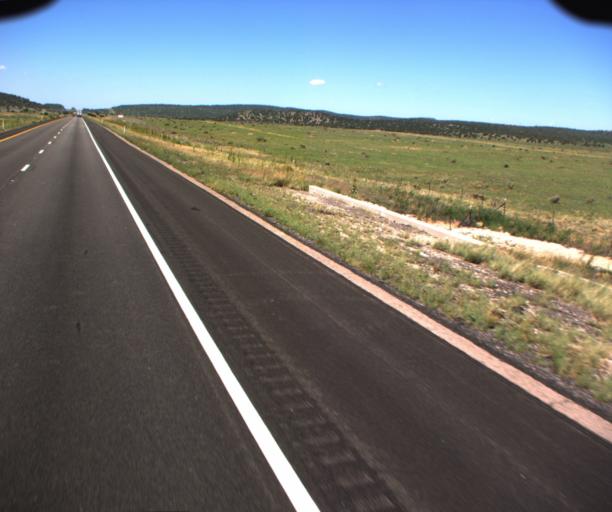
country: US
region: Arizona
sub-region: Mohave County
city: Peach Springs
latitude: 35.2606
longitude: -113.1637
